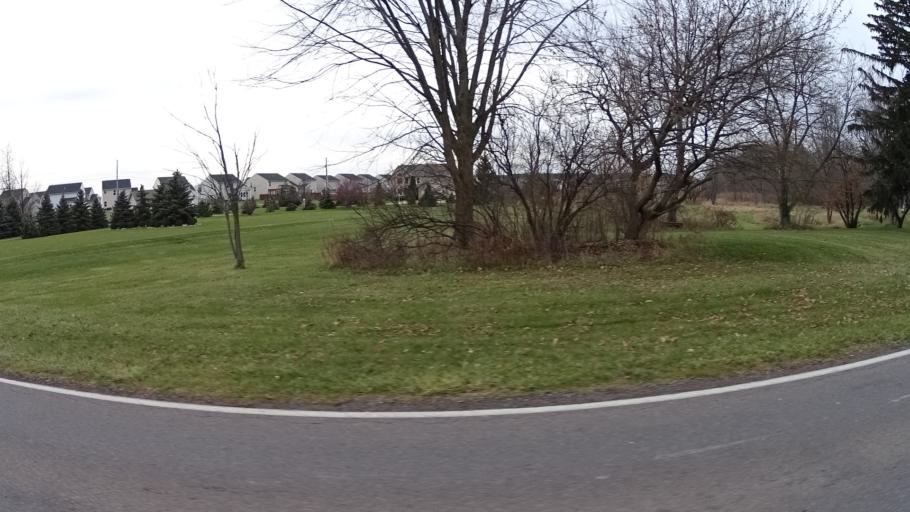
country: US
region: Ohio
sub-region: Lorain County
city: North Ridgeville
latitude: 41.3978
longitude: -82.0288
